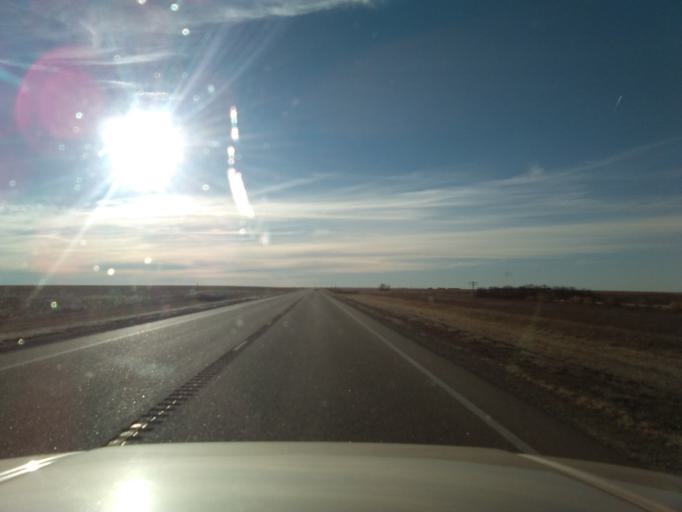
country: US
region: Kansas
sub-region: Sheridan County
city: Hoxie
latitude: 39.5209
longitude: -100.6217
